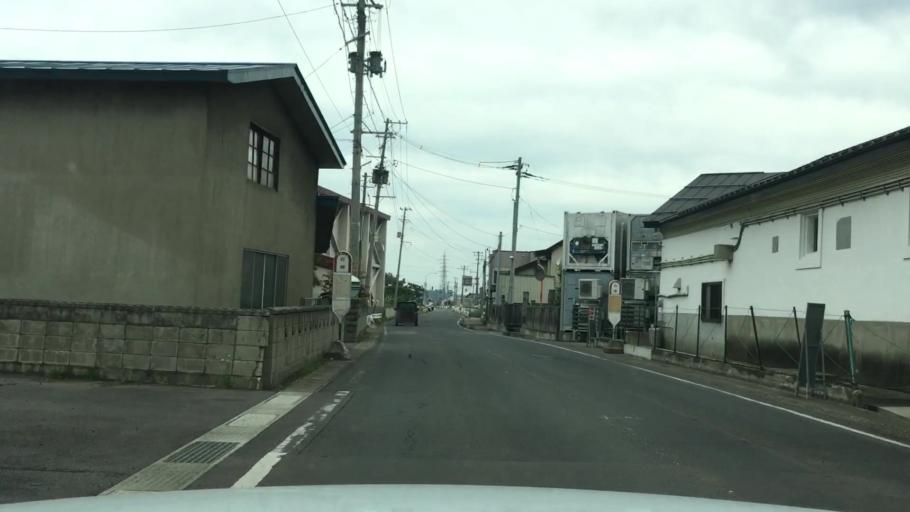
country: JP
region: Aomori
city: Hirosaki
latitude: 40.6292
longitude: 140.4533
